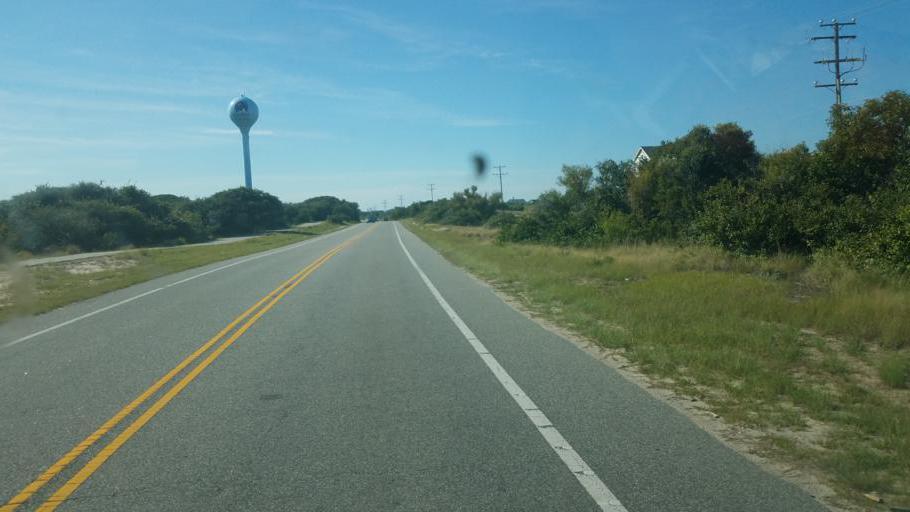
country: US
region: North Carolina
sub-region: Dare County
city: Southern Shores
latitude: 36.3085
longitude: -75.8080
